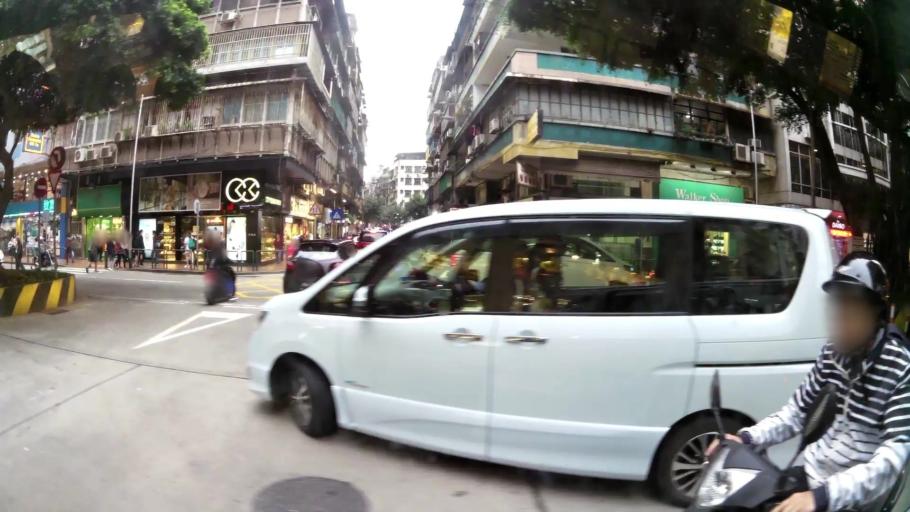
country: MO
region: Macau
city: Macau
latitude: 22.2039
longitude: 113.5461
